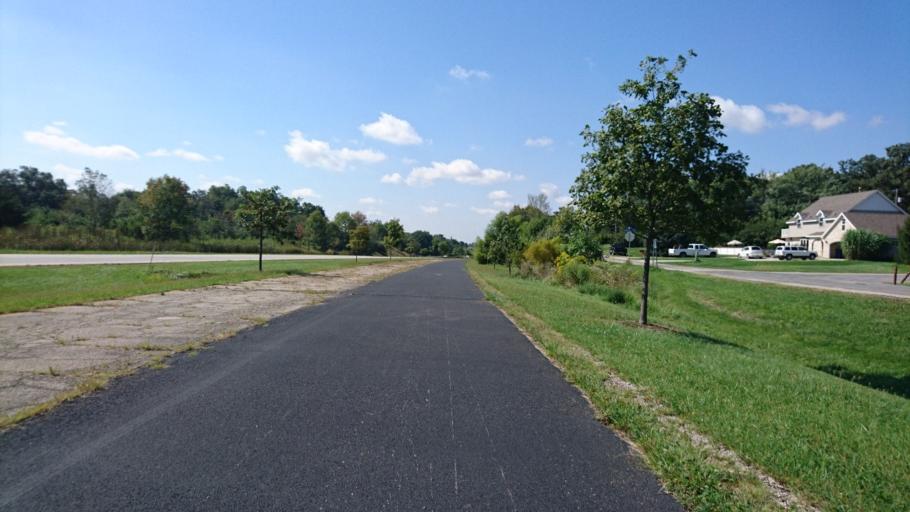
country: US
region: Illinois
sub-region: McLean County
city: Lexington
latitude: 40.6344
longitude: -88.7966
